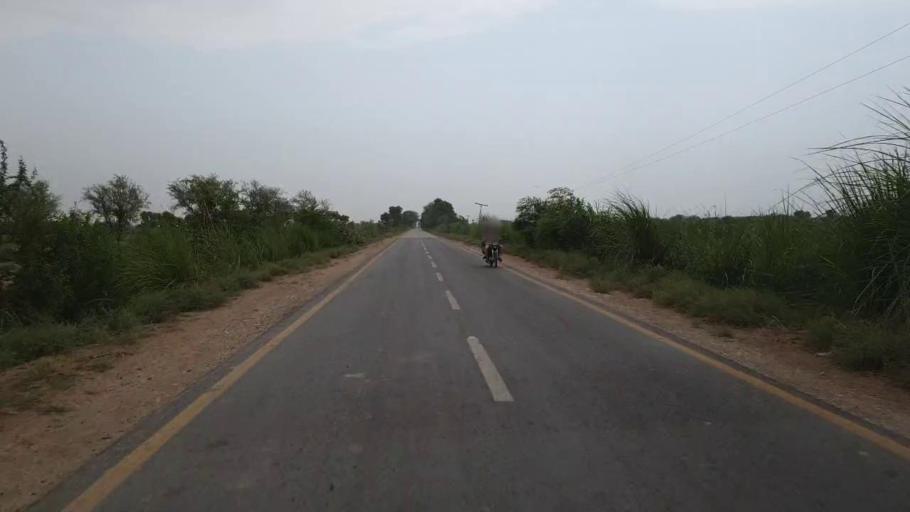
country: PK
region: Sindh
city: Bandhi
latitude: 26.5892
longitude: 68.2153
